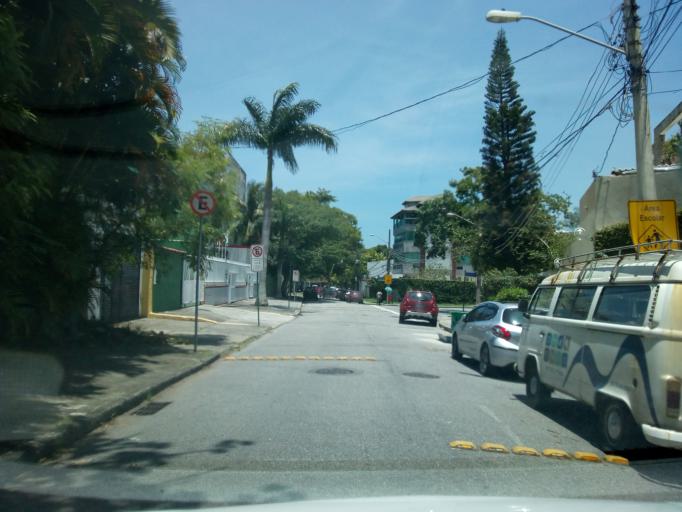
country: BR
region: Rio de Janeiro
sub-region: Rio De Janeiro
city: Rio de Janeiro
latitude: -23.0077
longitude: -43.2935
